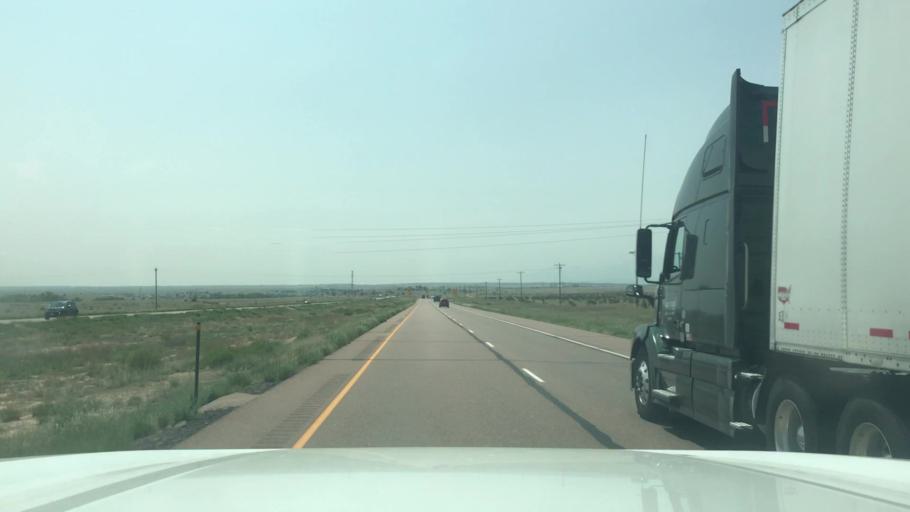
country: US
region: Colorado
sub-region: Pueblo County
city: Pueblo
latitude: 38.1384
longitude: -104.6631
